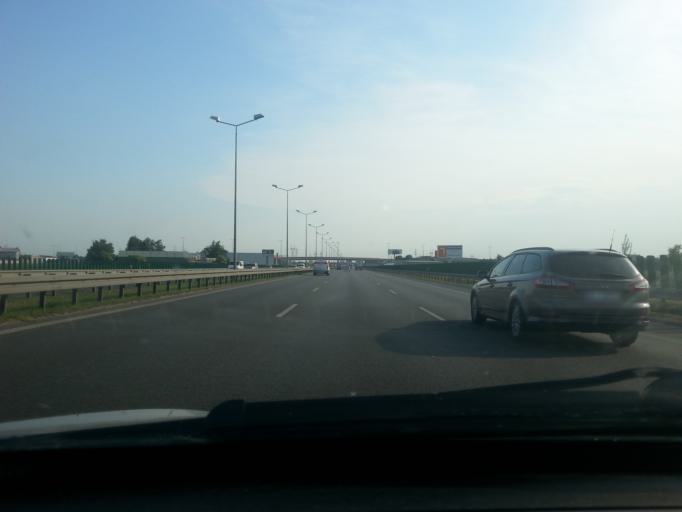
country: PL
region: Masovian Voivodeship
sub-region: Powiat warszawski zachodni
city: Babice
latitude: 52.2315
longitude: 20.8798
